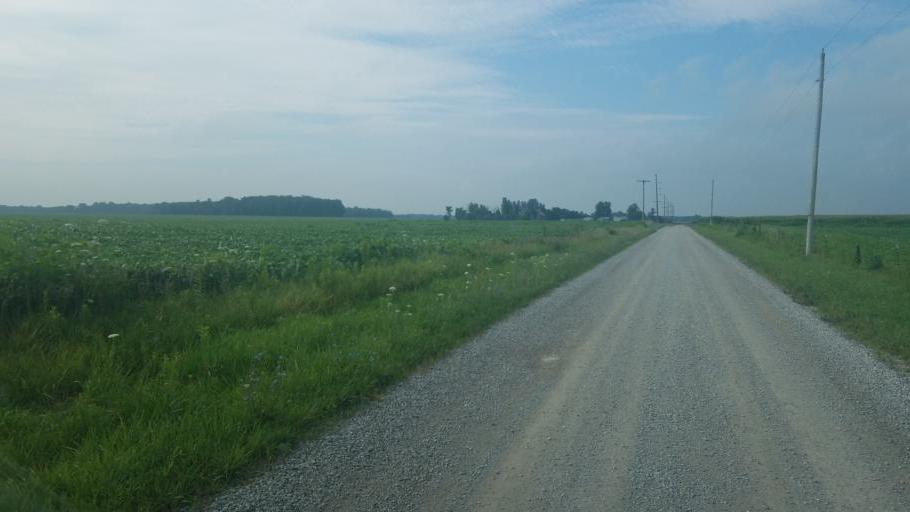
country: US
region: Ohio
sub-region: Delaware County
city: Ashley
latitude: 40.3879
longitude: -82.9120
